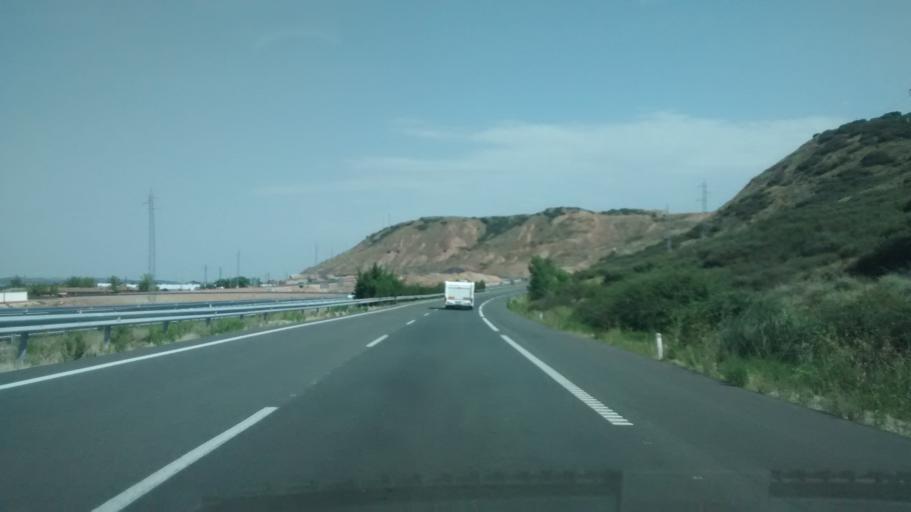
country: ES
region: La Rioja
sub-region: Provincia de La Rioja
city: Murillo de Rio Leza
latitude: 42.4475
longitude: -2.3486
